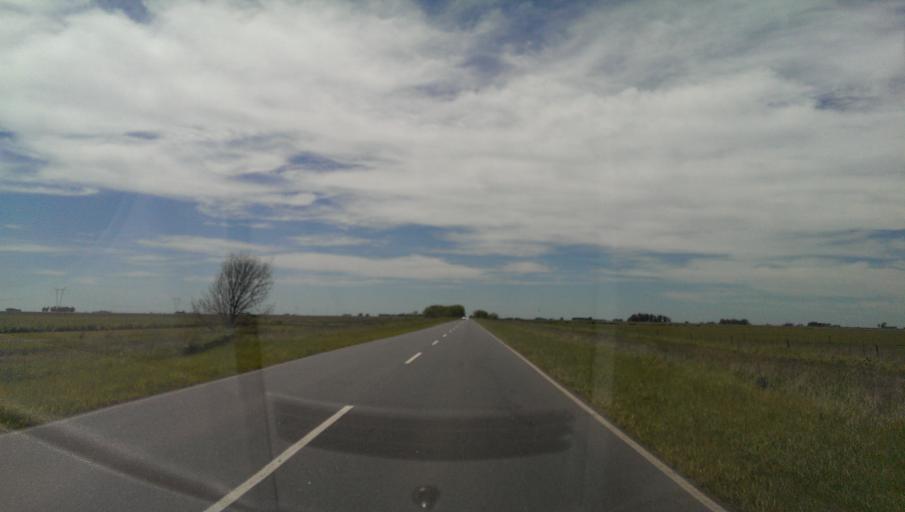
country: AR
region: Buenos Aires
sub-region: Partido de Laprida
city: Laprida
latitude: -37.2203
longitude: -60.6955
